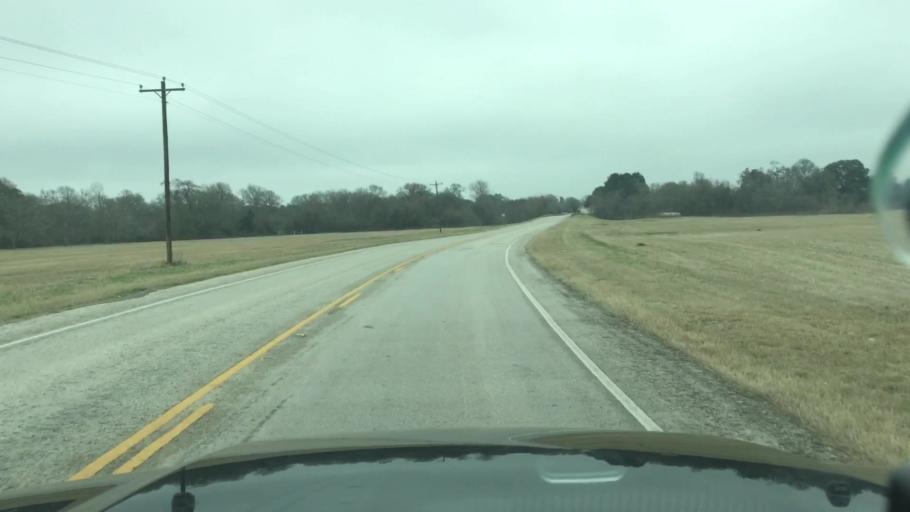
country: US
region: Texas
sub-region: Fayette County
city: La Grange
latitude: 30.0107
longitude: -96.9130
